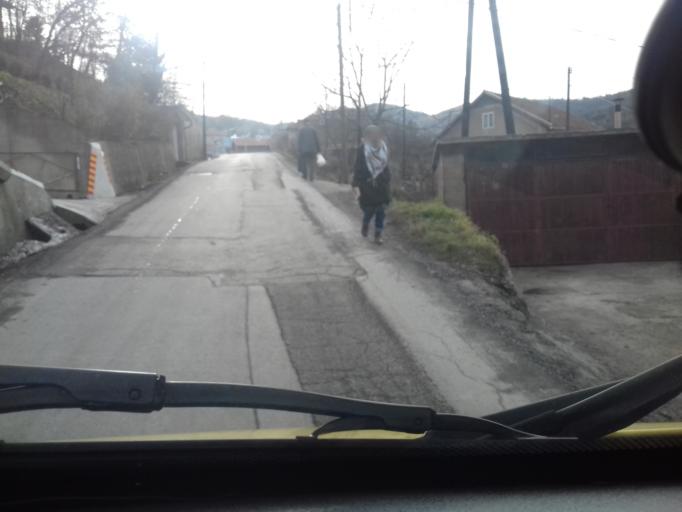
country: BA
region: Federation of Bosnia and Herzegovina
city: Zenica
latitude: 44.1890
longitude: 17.9080
